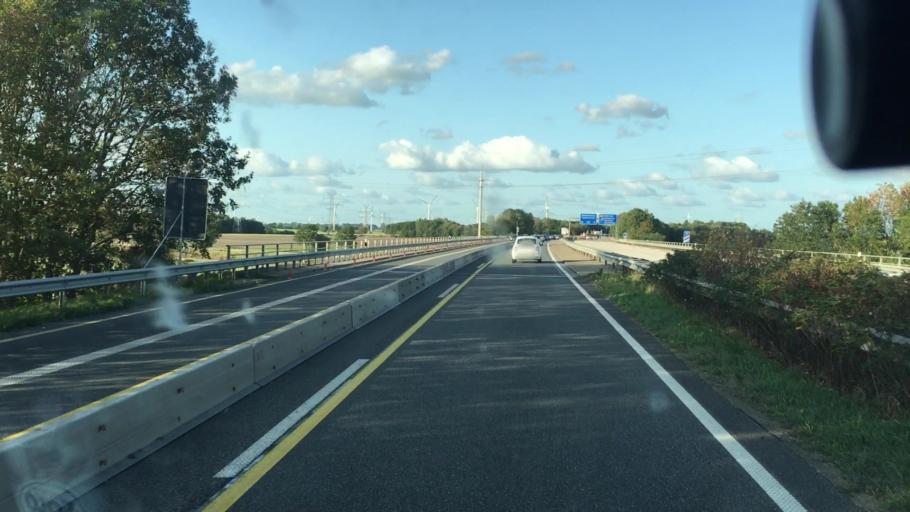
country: DE
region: Lower Saxony
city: Sande
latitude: 53.5177
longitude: 7.9987
